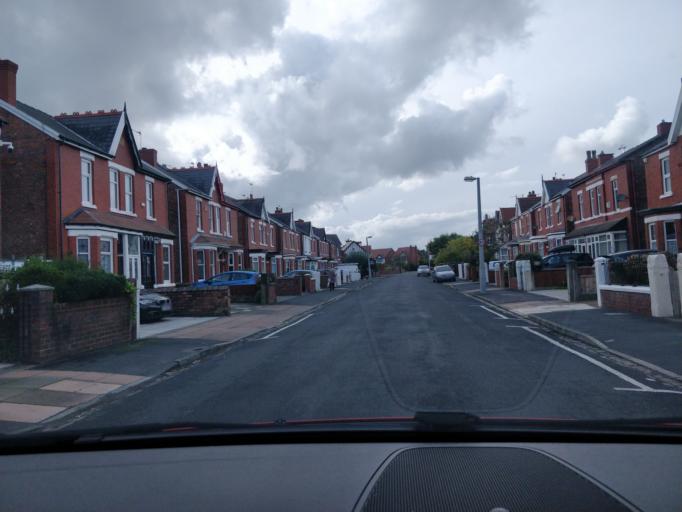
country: GB
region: England
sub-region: Sefton
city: Southport
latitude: 53.6224
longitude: -3.0156
